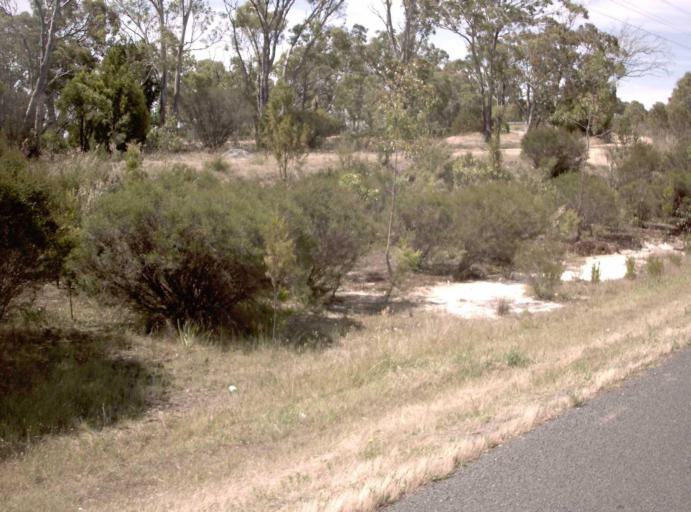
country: AU
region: Victoria
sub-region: Wellington
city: Sale
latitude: -37.9454
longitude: 147.1239
